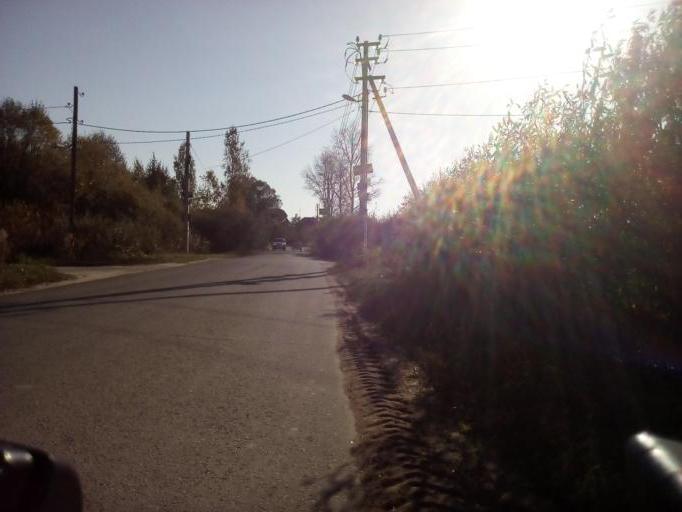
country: RU
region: Moskovskaya
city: Malyshevo
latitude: 55.5577
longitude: 38.3158
